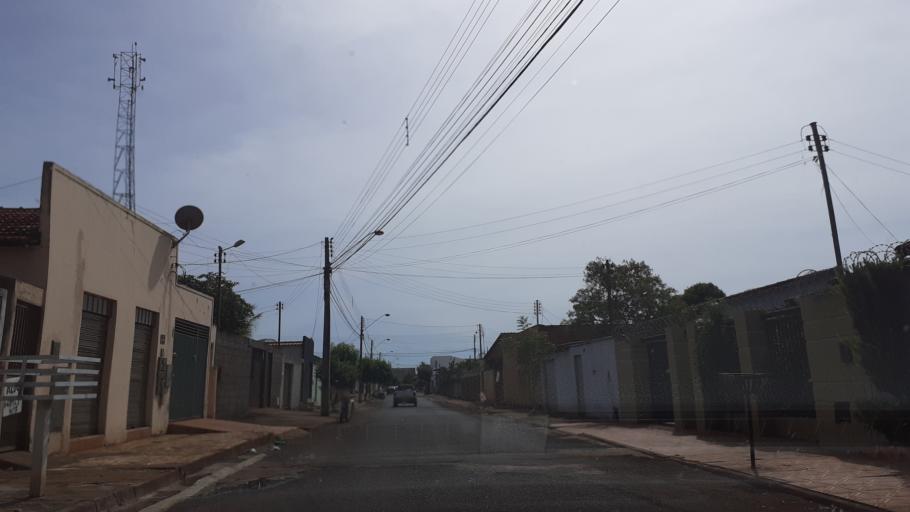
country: BR
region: Goias
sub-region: Itumbiara
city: Itumbiara
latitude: -18.4120
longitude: -49.2295
